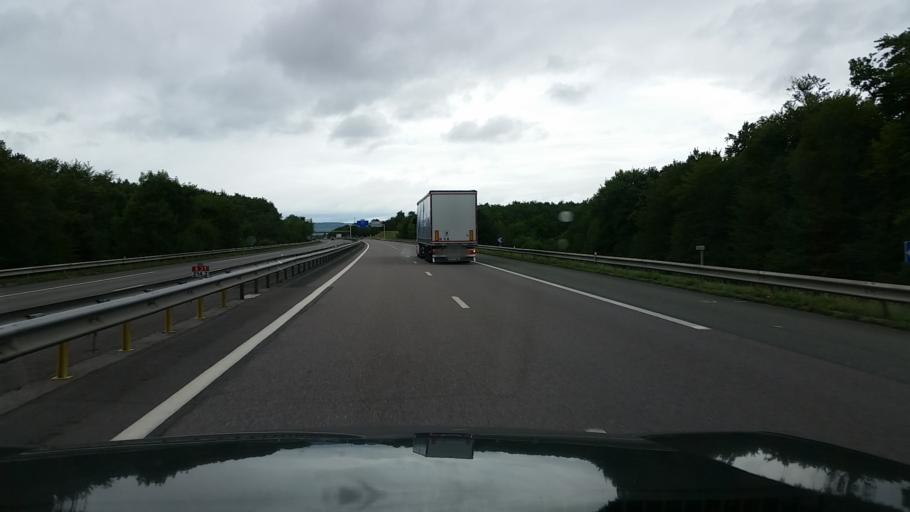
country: FR
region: Lorraine
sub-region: Departement de Meurthe-et-Moselle
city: Colombey-les-Belles
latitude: 48.5320
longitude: 5.9109
